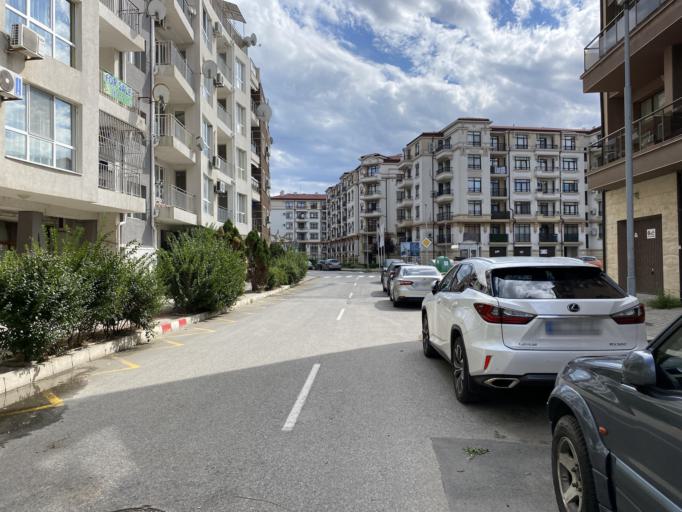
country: BG
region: Burgas
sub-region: Obshtina Pomorie
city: Pomorie
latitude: 42.5637
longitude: 27.6409
